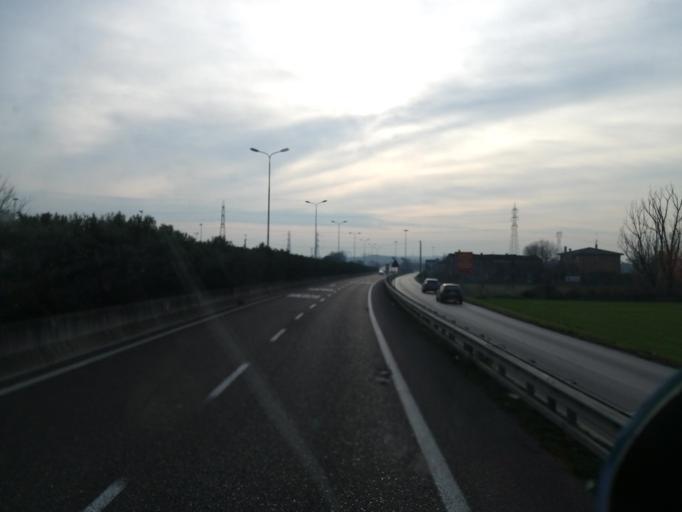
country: IT
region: Lombardy
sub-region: Provincia di Mantova
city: Castiglione delle Stiviere
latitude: 45.4260
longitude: 10.5154
